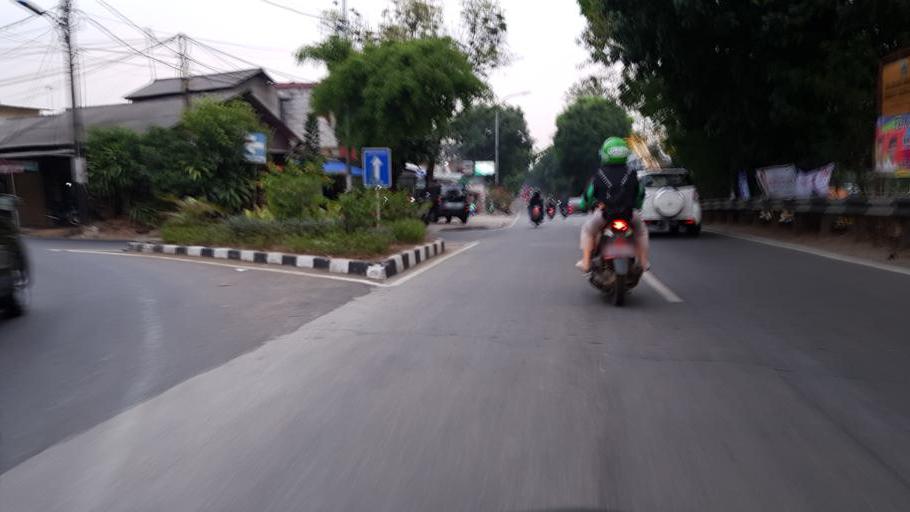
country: ID
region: Jakarta Raya
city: Jakarta
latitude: -6.3076
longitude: 106.8954
